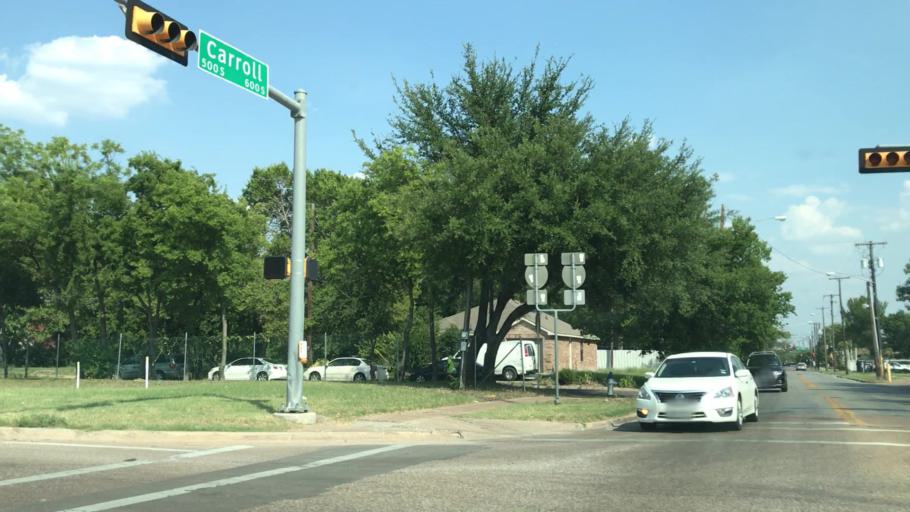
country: US
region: Texas
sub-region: Dallas County
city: Dallas
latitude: 32.7884
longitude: -96.7639
